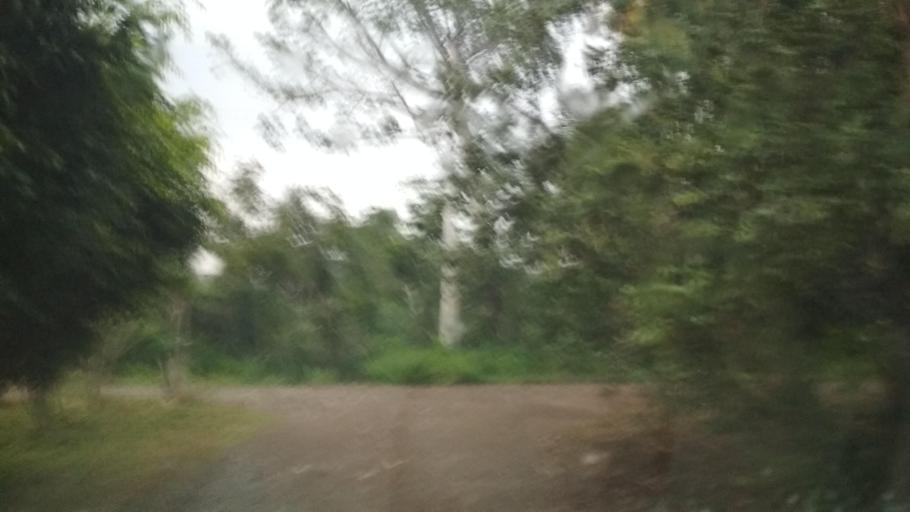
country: MM
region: Shan
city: Taunggyi
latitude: 20.3046
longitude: 97.3063
